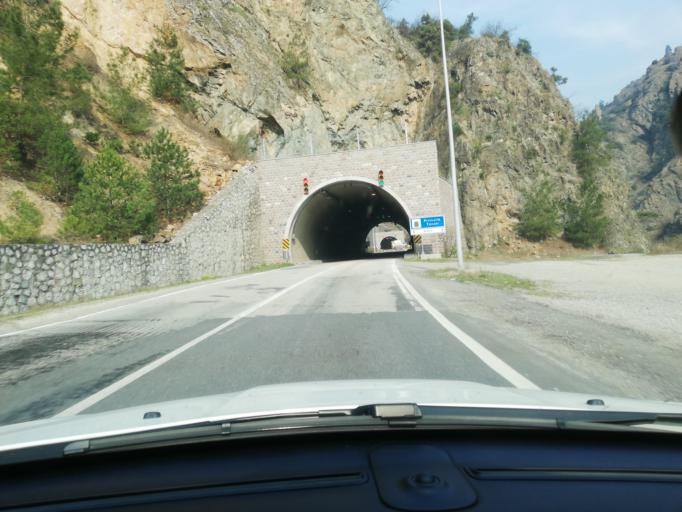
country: TR
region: Karabuk
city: Karabuk
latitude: 41.1519
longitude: 32.5297
